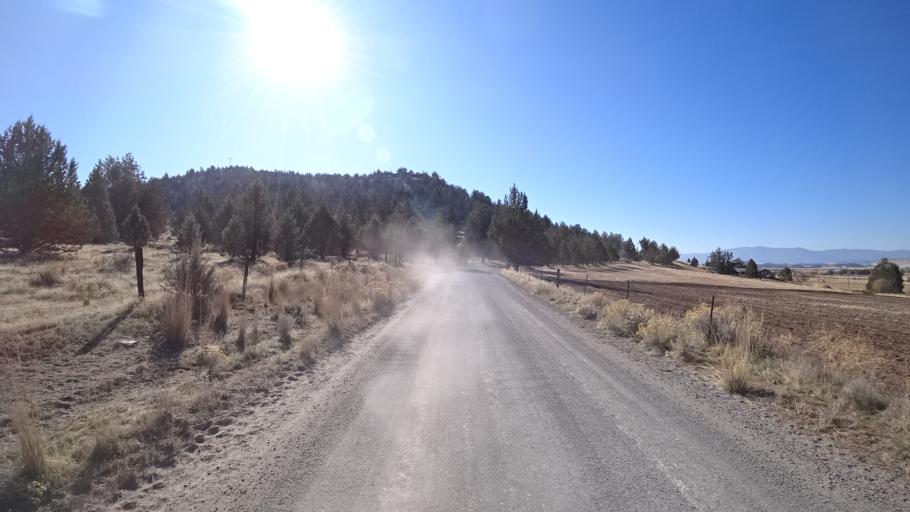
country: US
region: California
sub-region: Siskiyou County
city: Montague
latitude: 41.7158
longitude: -122.3728
